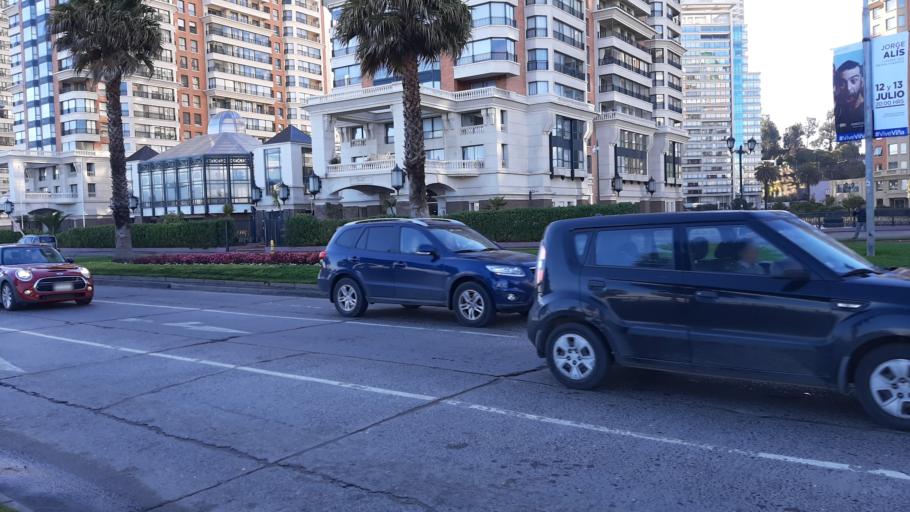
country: CL
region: Valparaiso
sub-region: Provincia de Valparaiso
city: Vina del Mar
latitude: -33.0073
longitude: -71.5509
